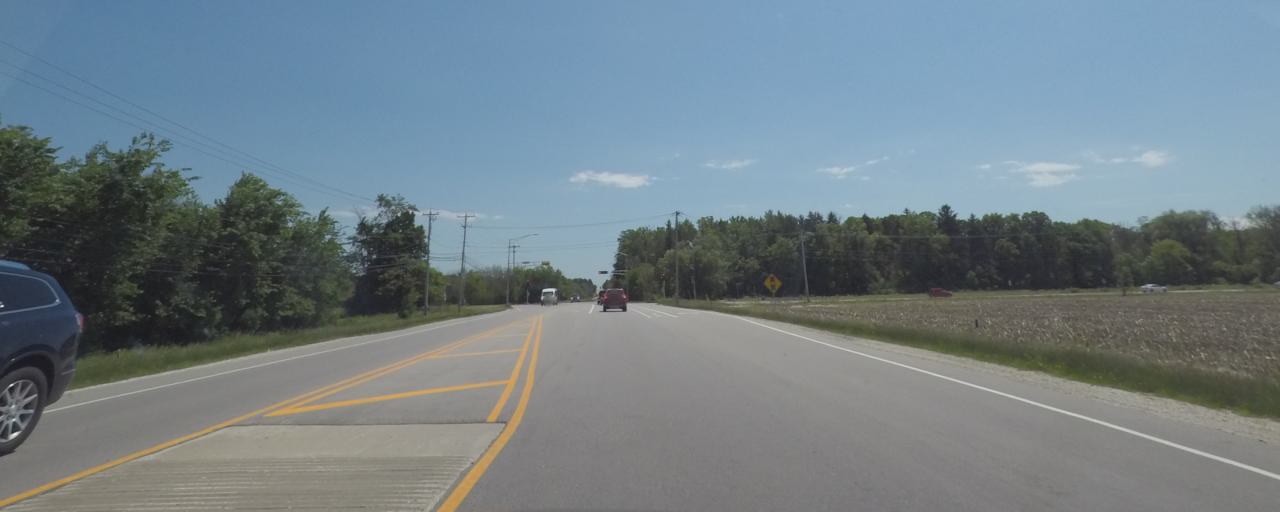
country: US
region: Wisconsin
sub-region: Waukesha County
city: New Berlin
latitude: 42.9819
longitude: -88.1283
